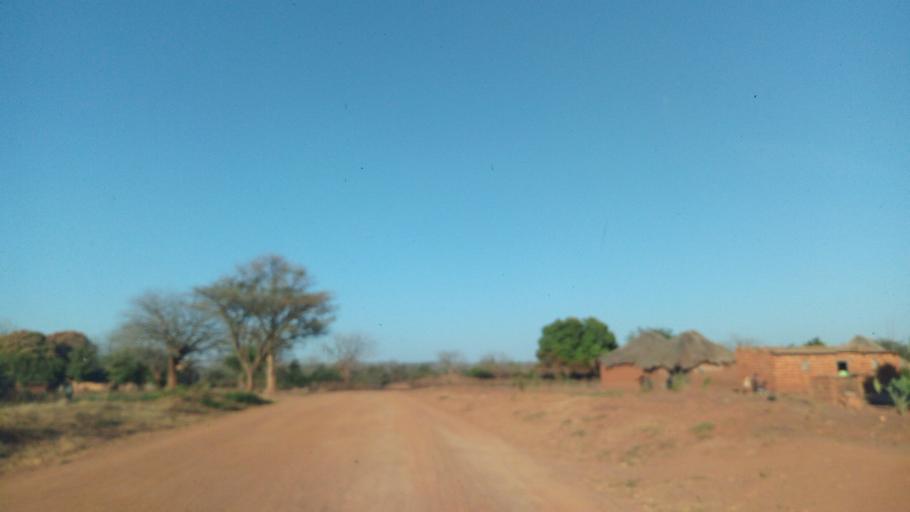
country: ZM
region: Luapula
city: Mwense
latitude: -10.4060
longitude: 28.6161
